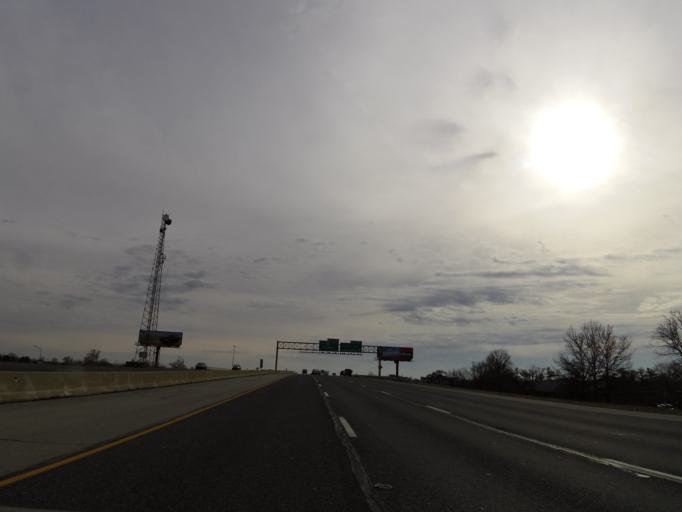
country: US
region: Indiana
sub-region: Marion County
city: Lawrence
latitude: 39.8978
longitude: -86.0589
